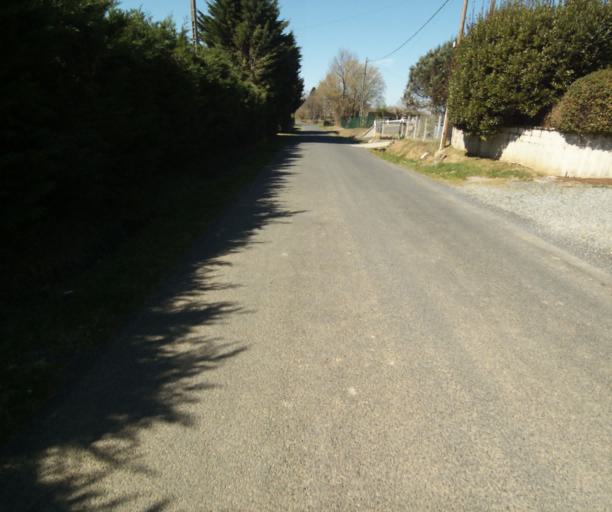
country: FR
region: Limousin
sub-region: Departement de la Correze
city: Chamboulive
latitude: 45.4383
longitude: 1.6891
